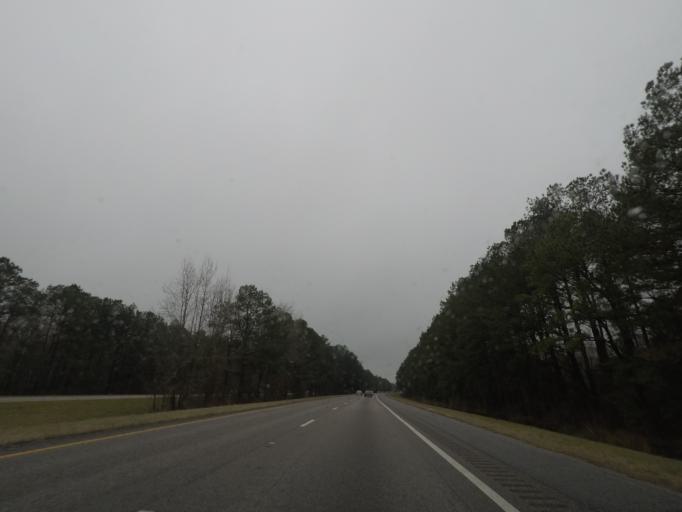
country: US
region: South Carolina
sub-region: Florence County
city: Timmonsville
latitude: 33.9947
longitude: -80.0131
